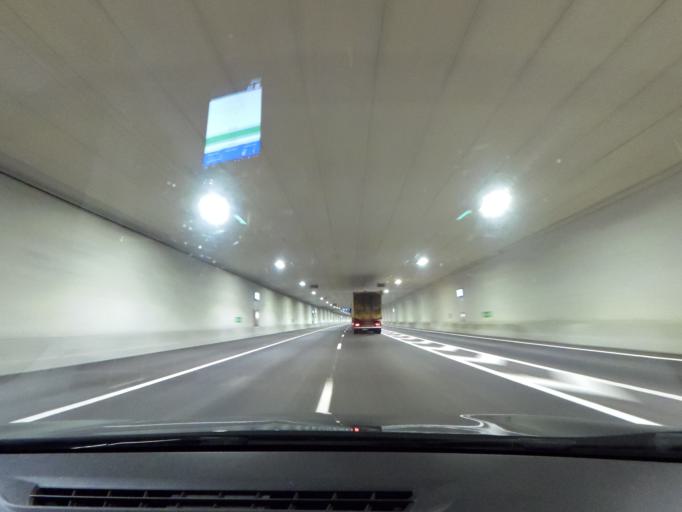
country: NL
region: South Holland
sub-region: Gemeente Schiedam
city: Schiedam
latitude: 51.9372
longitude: 4.3627
